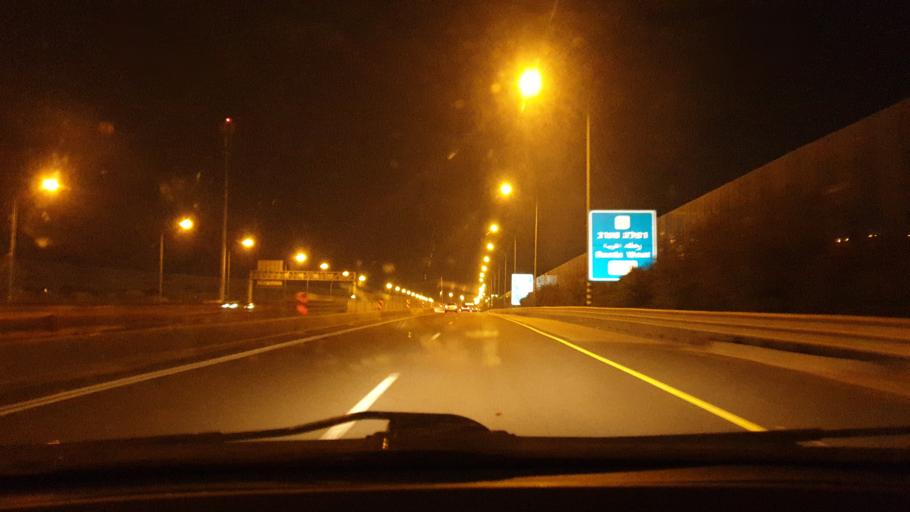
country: IL
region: Central District
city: Ramla
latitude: 31.9188
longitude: 34.8559
